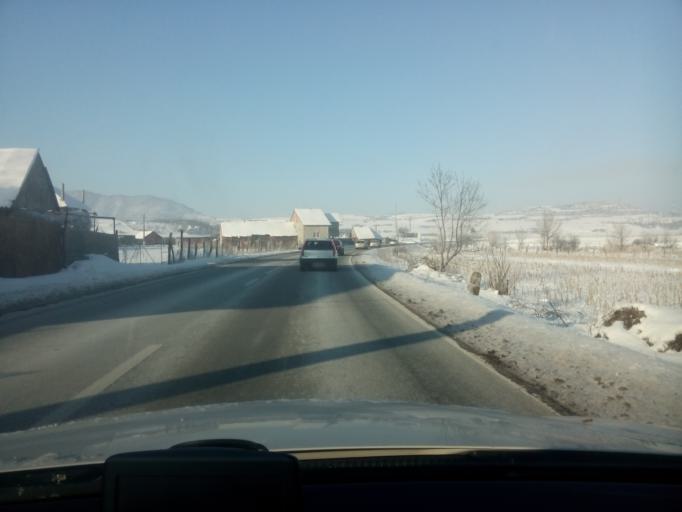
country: RO
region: Sibiu
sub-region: Comuna Boita
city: Boita
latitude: 45.6356
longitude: 24.2607
